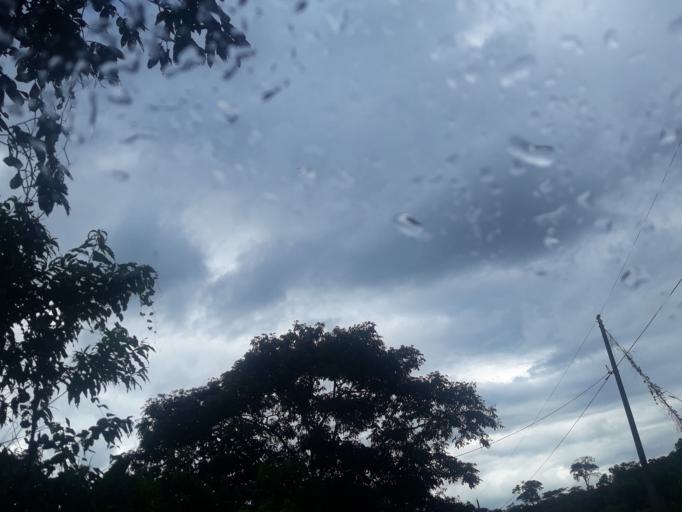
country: EC
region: Napo
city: Tena
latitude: -1.1003
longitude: -77.6842
